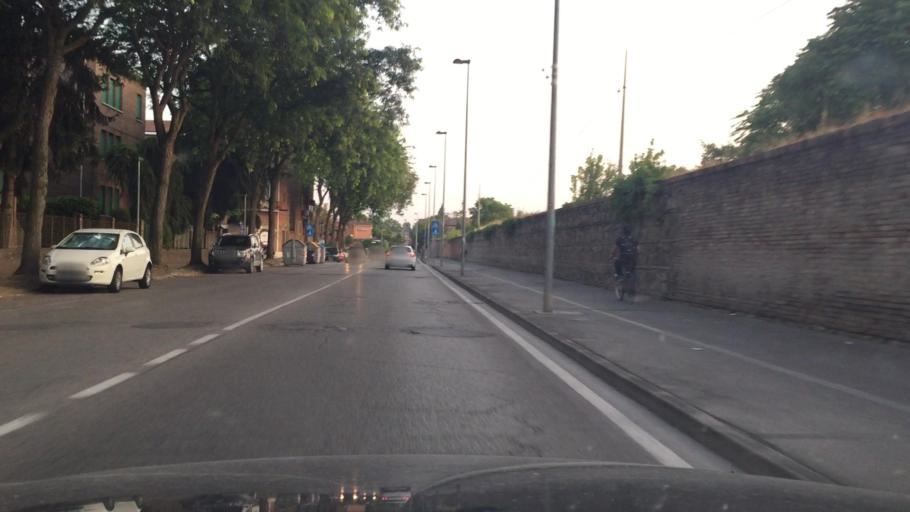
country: IT
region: Emilia-Romagna
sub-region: Provincia di Ferrara
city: Ferrara
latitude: 44.8404
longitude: 11.6026
